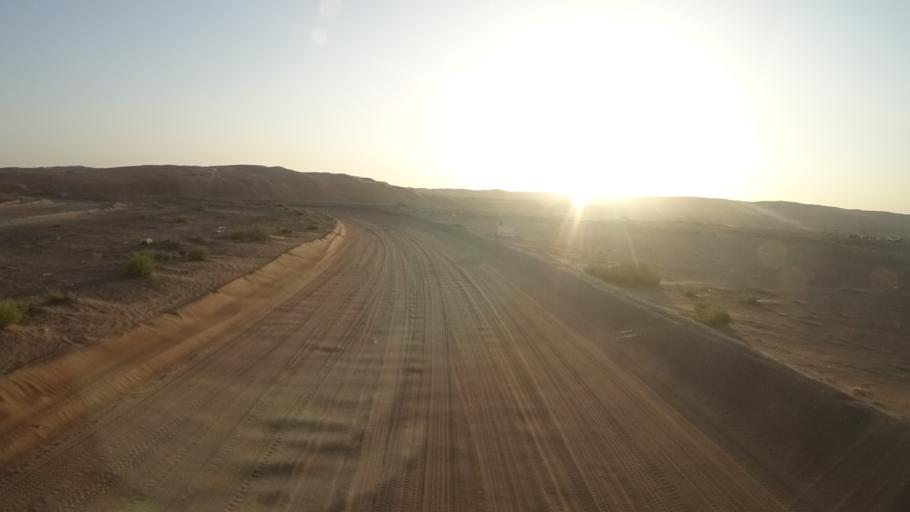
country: OM
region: Ash Sharqiyah
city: Al Qabil
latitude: 22.4966
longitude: 58.7305
